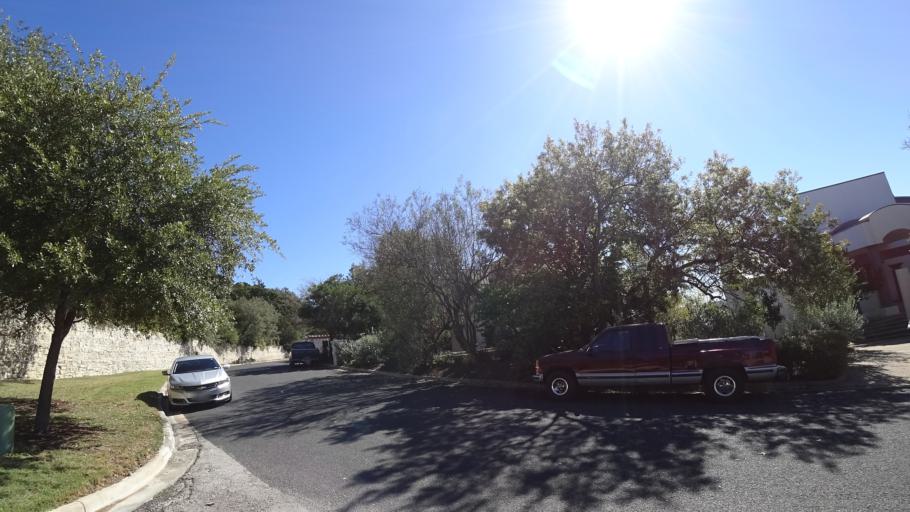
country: US
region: Texas
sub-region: Travis County
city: West Lake Hills
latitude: 30.3512
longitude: -97.7814
